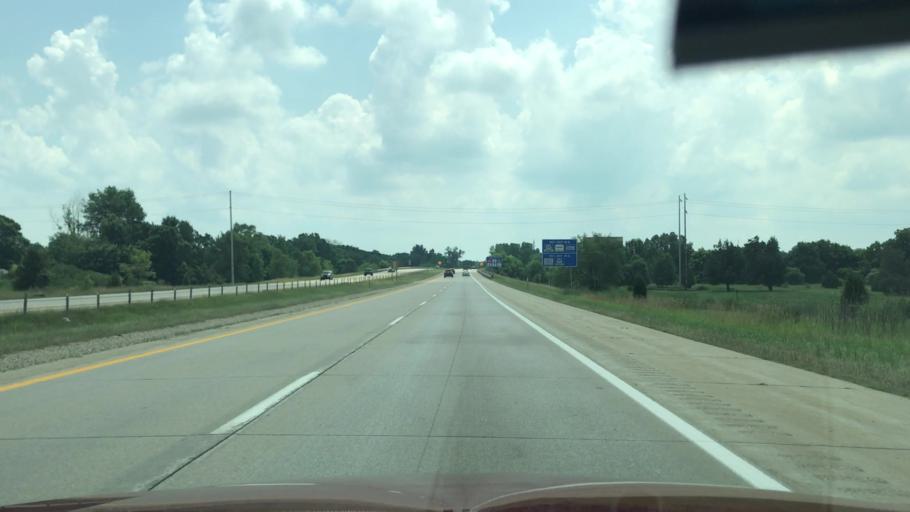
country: US
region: Michigan
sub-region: Allegan County
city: Plainwell
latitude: 42.4643
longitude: -85.6529
